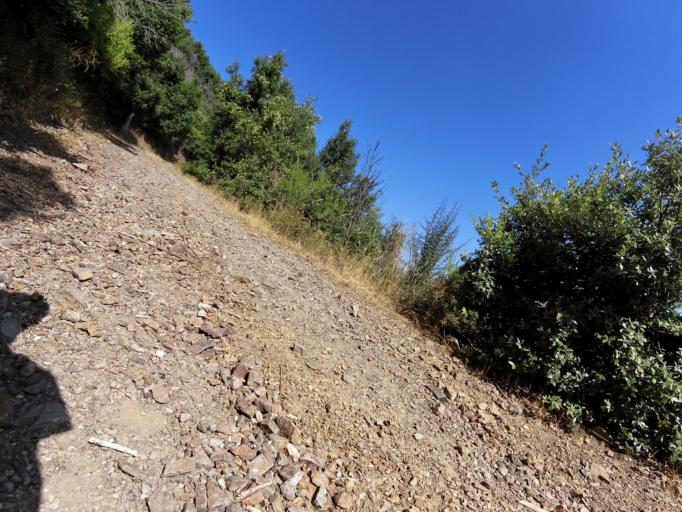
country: IT
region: Calabria
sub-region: Provincia di Reggio Calabria
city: Bivongi
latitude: 38.5011
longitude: 16.4488
